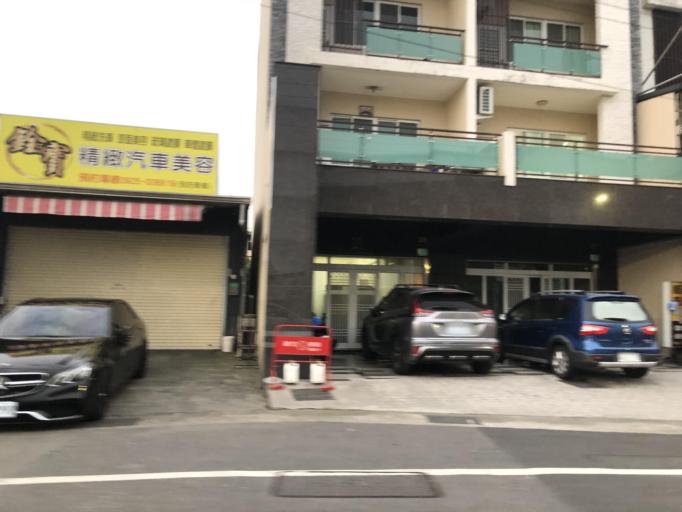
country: TW
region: Taiwan
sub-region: Tainan
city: Tainan
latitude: 23.0207
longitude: 120.2763
